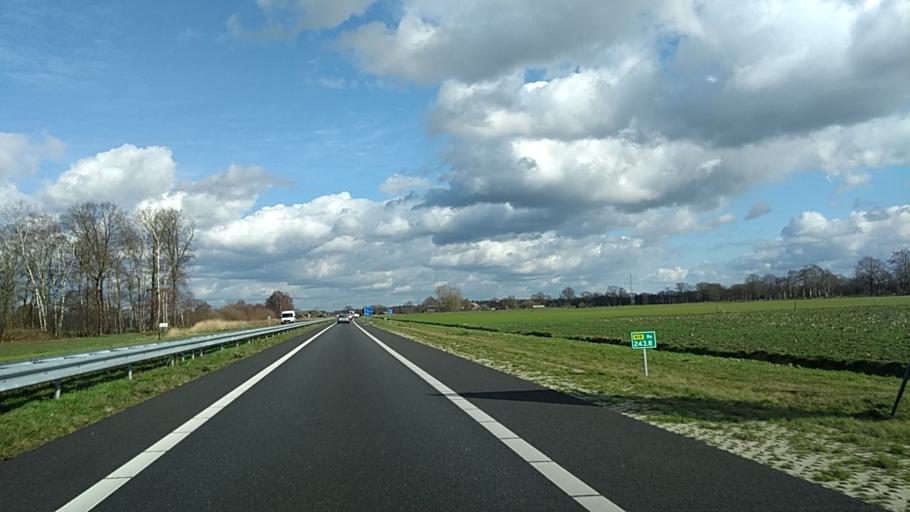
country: NL
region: Gelderland
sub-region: Berkelland
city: Eibergen
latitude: 52.1263
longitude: 6.6535
